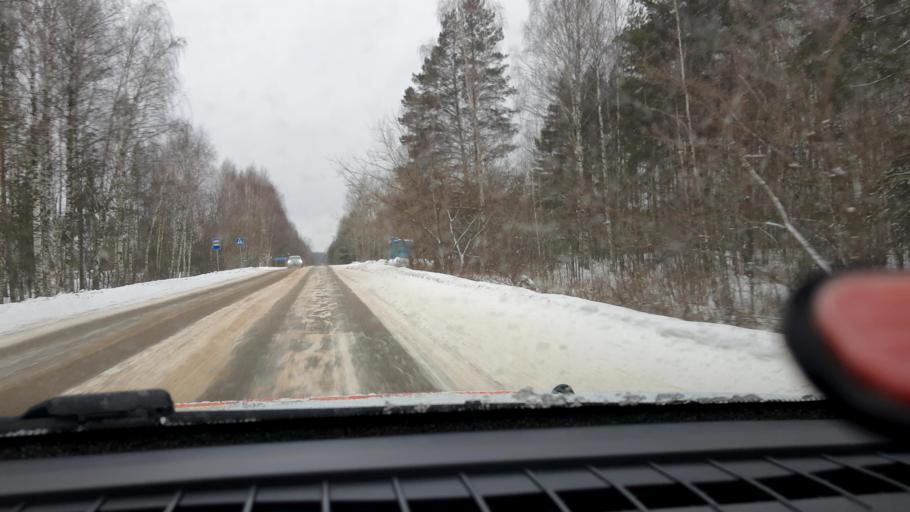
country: RU
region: Nizjnij Novgorod
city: Pamyat' Parizhskoy Kommuny
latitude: 56.2726
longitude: 44.4094
